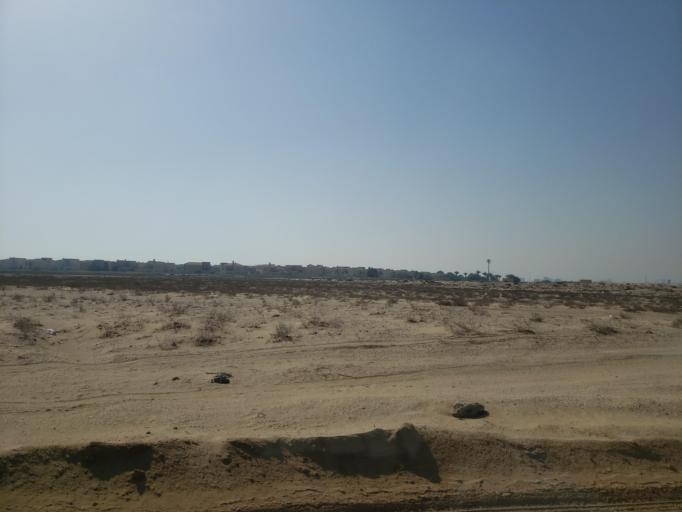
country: AE
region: Umm al Qaywayn
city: Umm al Qaywayn
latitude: 25.5294
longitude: 55.5915
